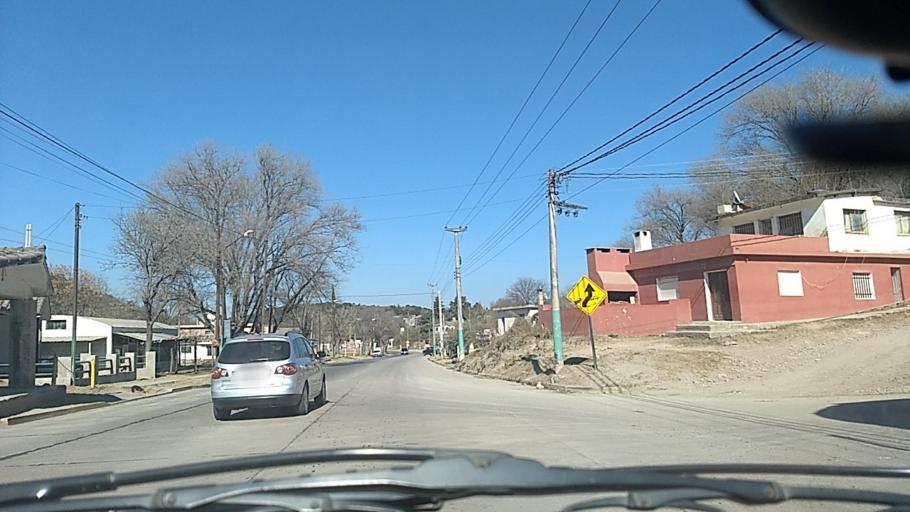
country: AR
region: Cordoba
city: Salsipuedes
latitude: -31.1045
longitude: -64.2921
